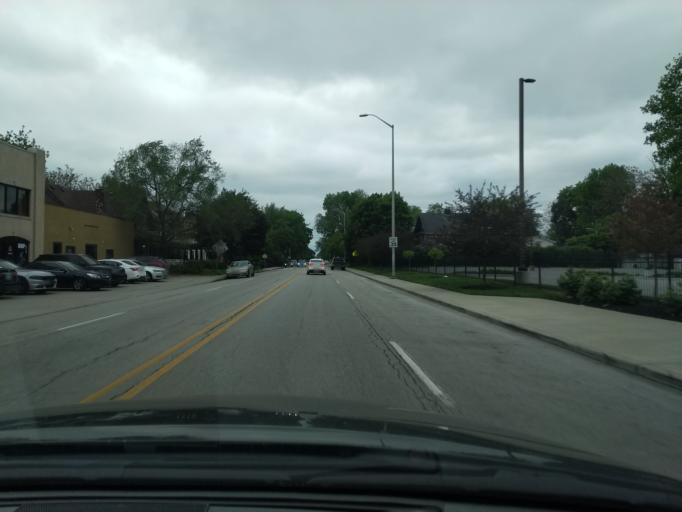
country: US
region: Indiana
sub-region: Marion County
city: Indianapolis
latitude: 39.8172
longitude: -86.1497
